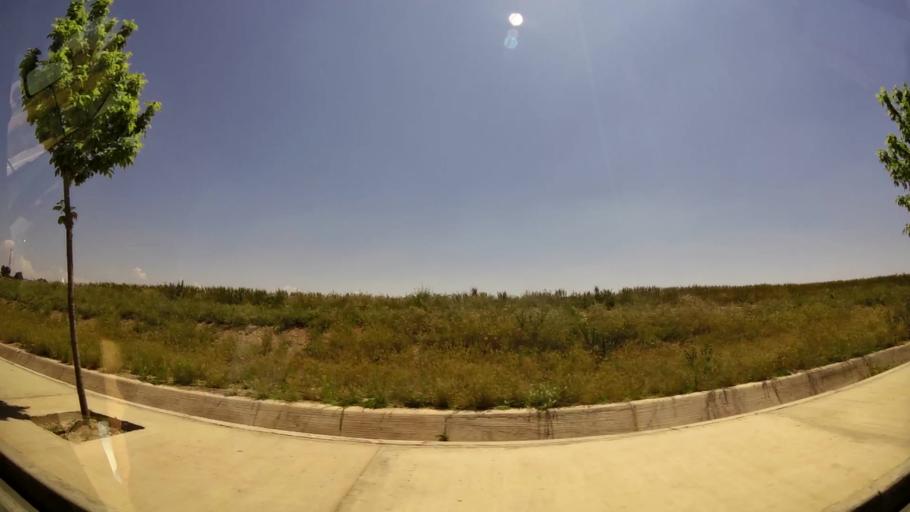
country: MA
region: Oriental
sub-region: Oujda-Angad
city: Oujda
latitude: 34.6940
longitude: -1.9259
